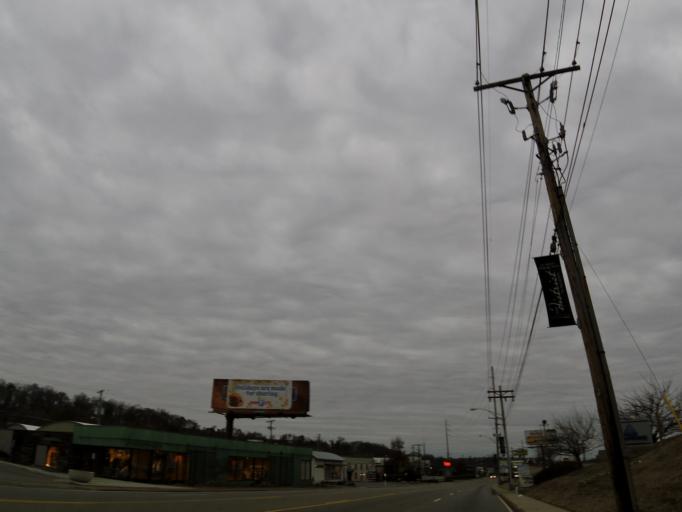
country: US
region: Tennessee
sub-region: Knox County
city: Knoxville
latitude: 35.9367
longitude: -83.9915
